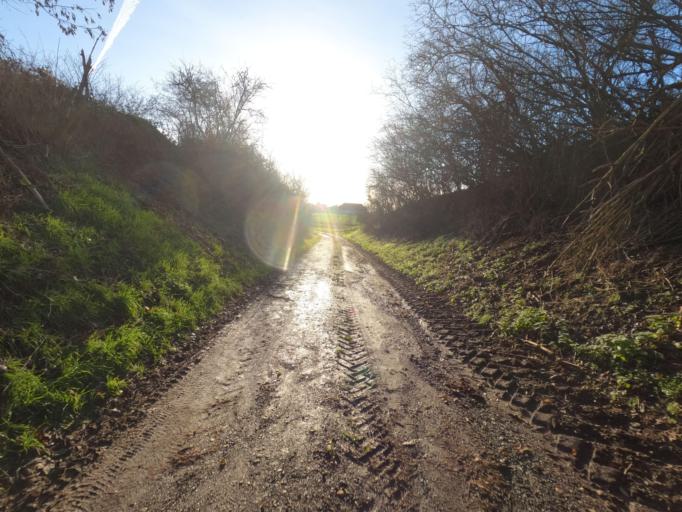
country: DE
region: North Rhine-Westphalia
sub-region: Regierungsbezirk Koln
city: Elsdorf
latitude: 50.9639
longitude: 6.5168
